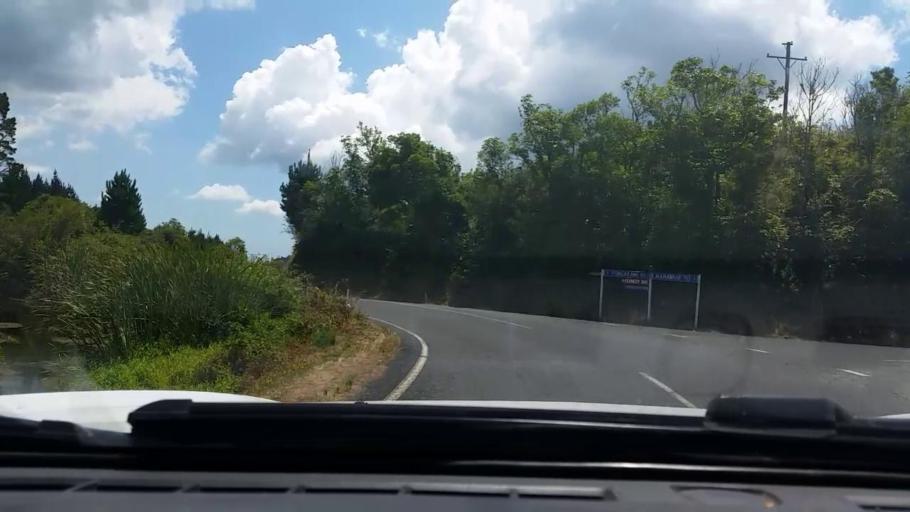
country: NZ
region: Bay of Plenty
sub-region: Kawerau District
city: Kawerau
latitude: -38.0367
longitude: 176.5493
